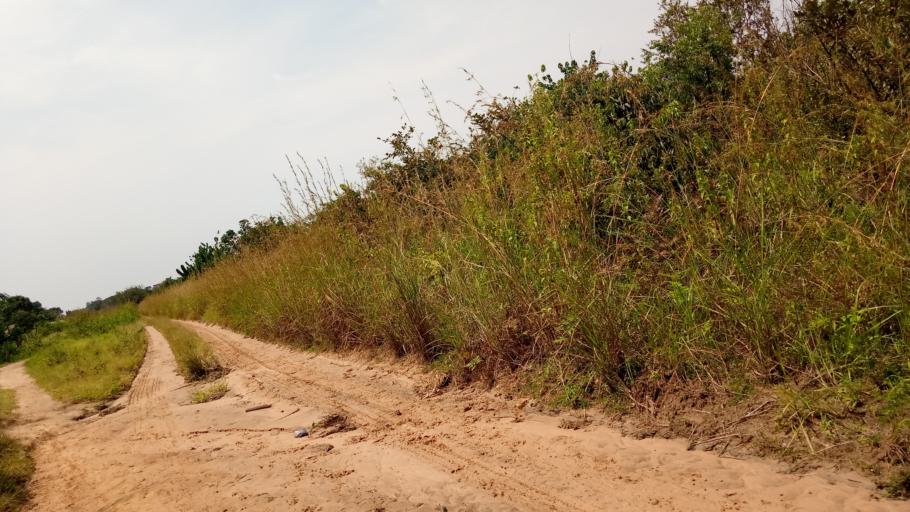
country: CD
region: Bandundu
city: Bandundu
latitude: -4.1723
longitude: 17.3952
